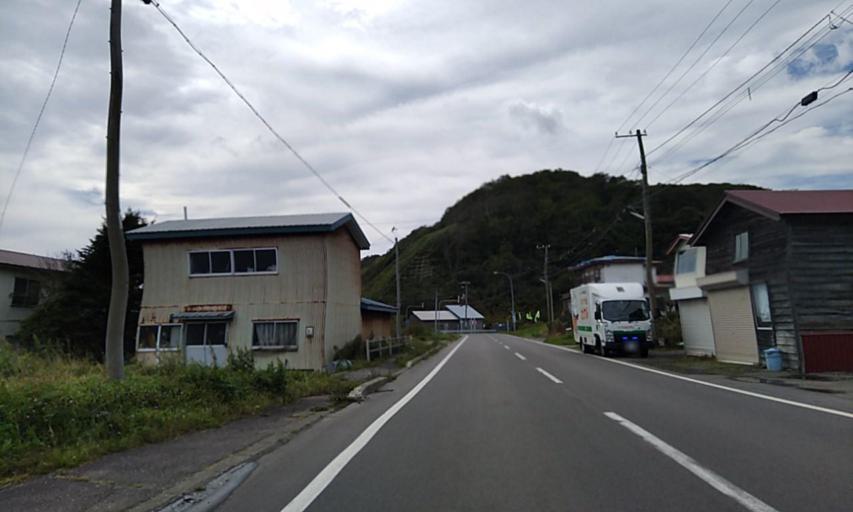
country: JP
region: Hokkaido
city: Kushiro
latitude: 42.7995
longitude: 143.8104
